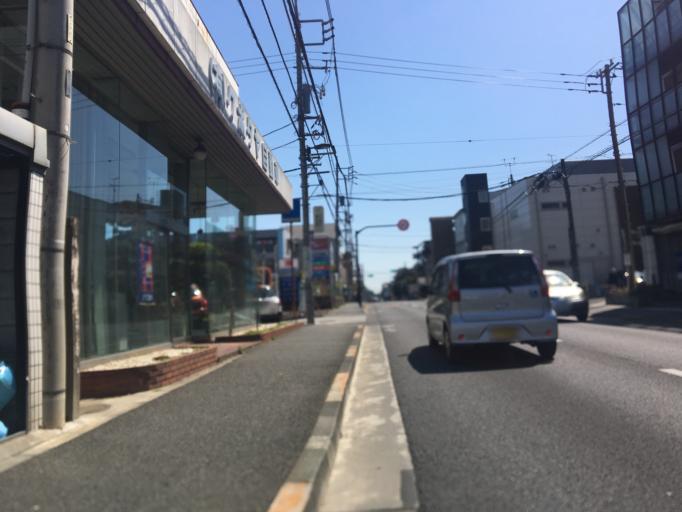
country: JP
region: Tokyo
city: Higashimurayama-shi
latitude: 35.7307
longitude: 139.4887
